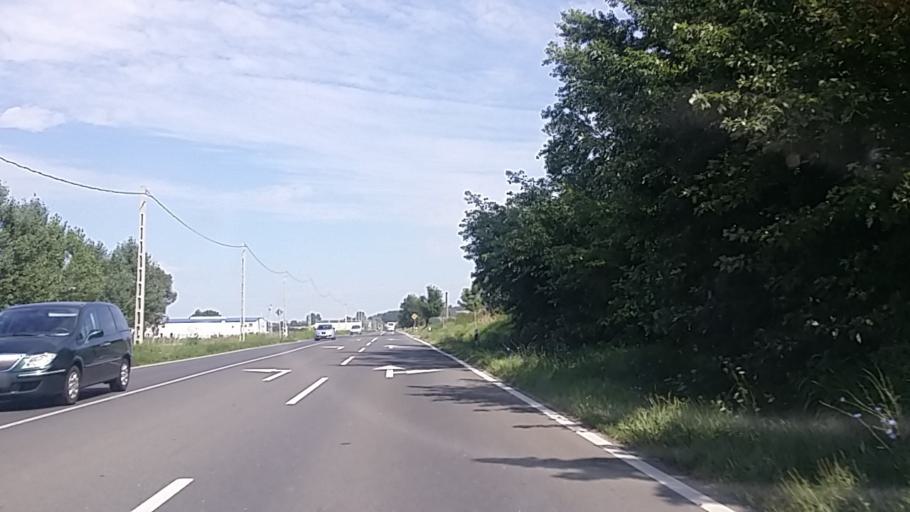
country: HU
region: Baranya
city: Sasd
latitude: 46.2378
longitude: 18.1210
